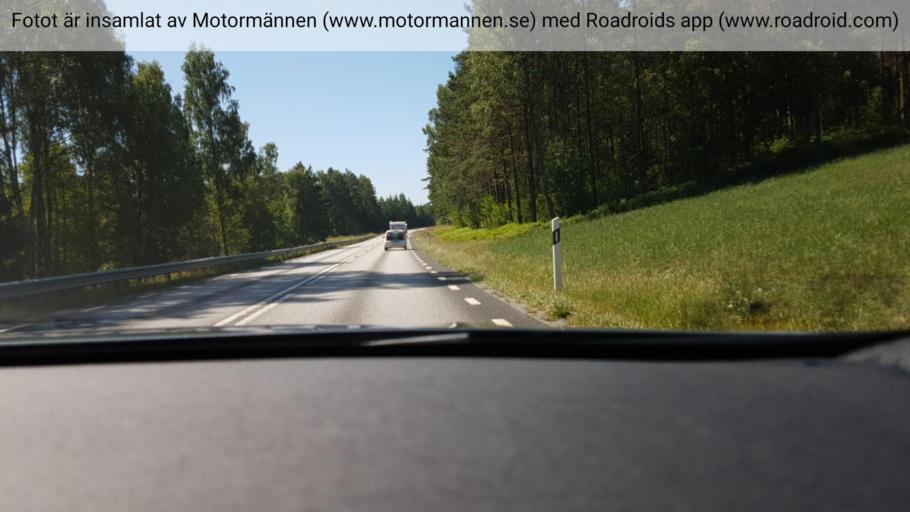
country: SE
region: Joenkoeping
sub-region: Gnosjo Kommun
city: Gnosjoe
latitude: 57.5213
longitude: 13.6838
